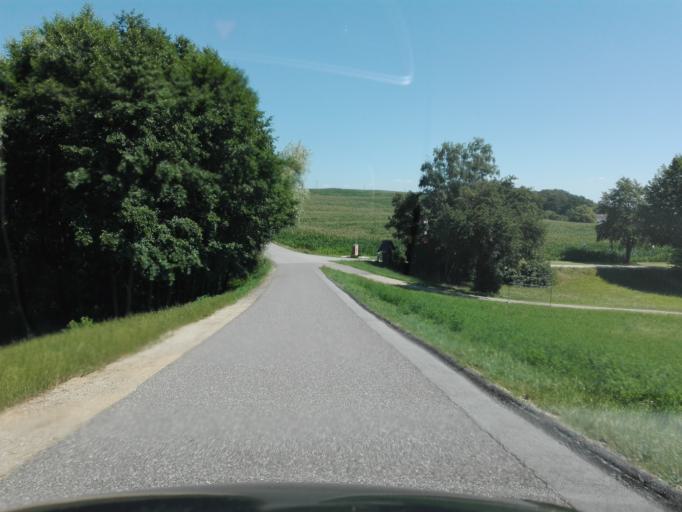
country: AT
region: Upper Austria
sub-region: Politischer Bezirk Urfahr-Umgebung
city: Steyregg
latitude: 48.3236
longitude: 14.3726
